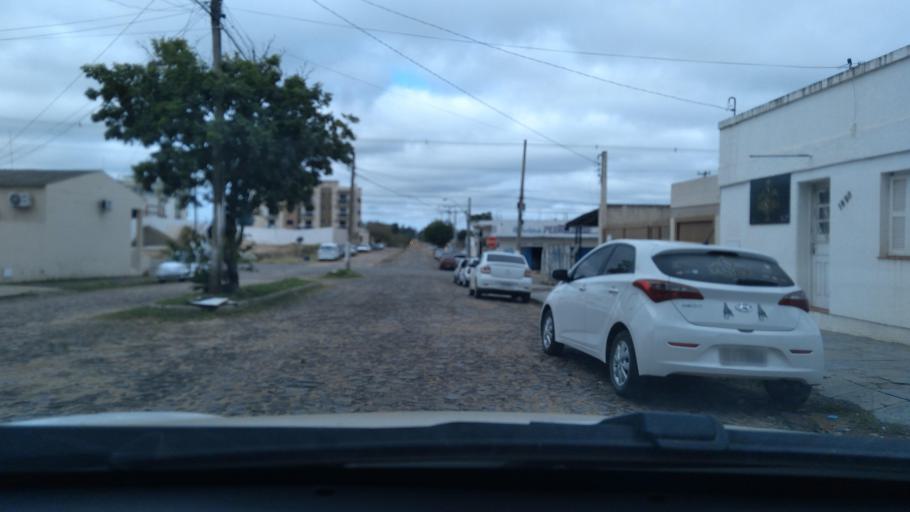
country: BR
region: Rio Grande do Sul
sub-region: Dom Pedrito
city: Dom Pedrito
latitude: -30.9814
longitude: -54.6669
